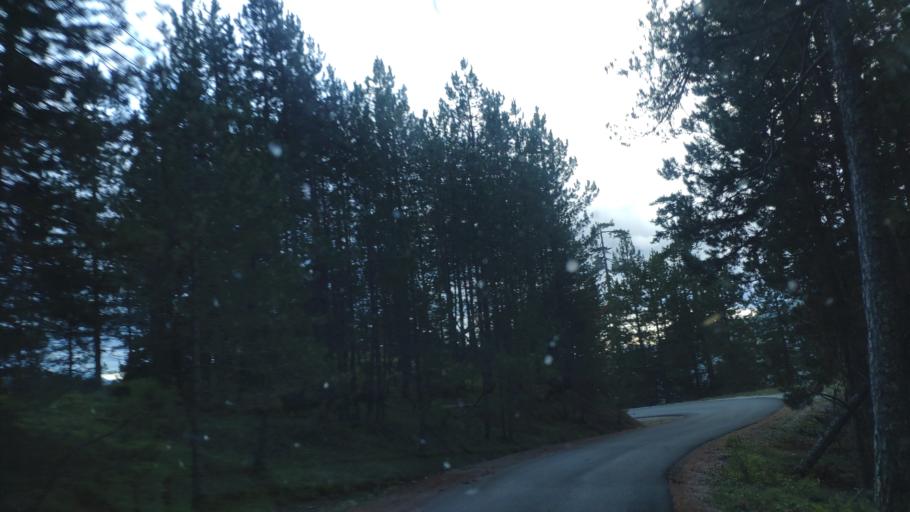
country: AL
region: Korce
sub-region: Rrethi i Kolonjes
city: Erseke
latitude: 40.2910
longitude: 20.8630
